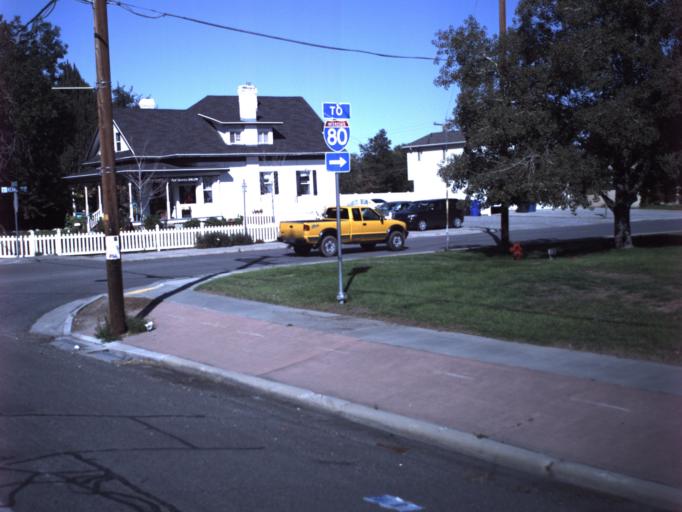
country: US
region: Utah
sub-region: Tooele County
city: Grantsville
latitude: 40.5999
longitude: -112.4576
